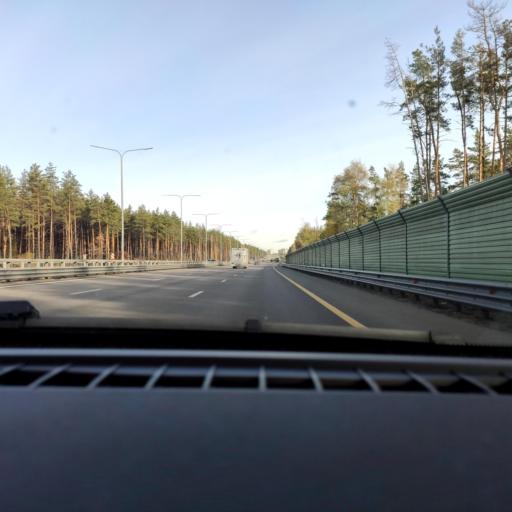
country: RU
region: Voronezj
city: Somovo
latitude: 51.7130
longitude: 39.3080
